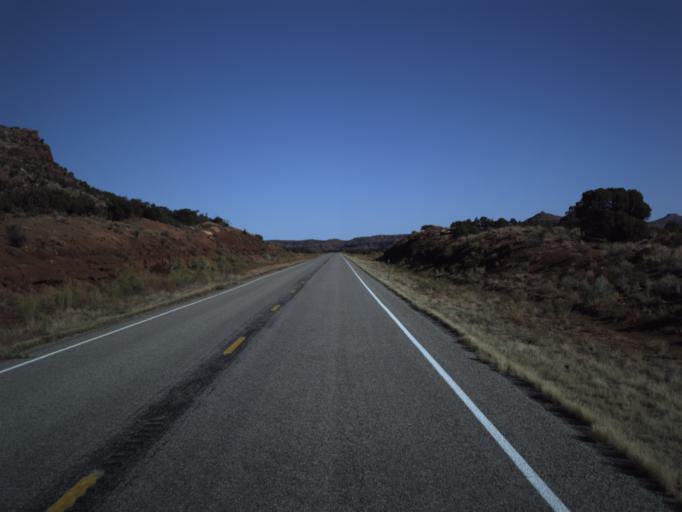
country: US
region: Utah
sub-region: San Juan County
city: Blanding
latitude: 37.6195
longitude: -110.0840
